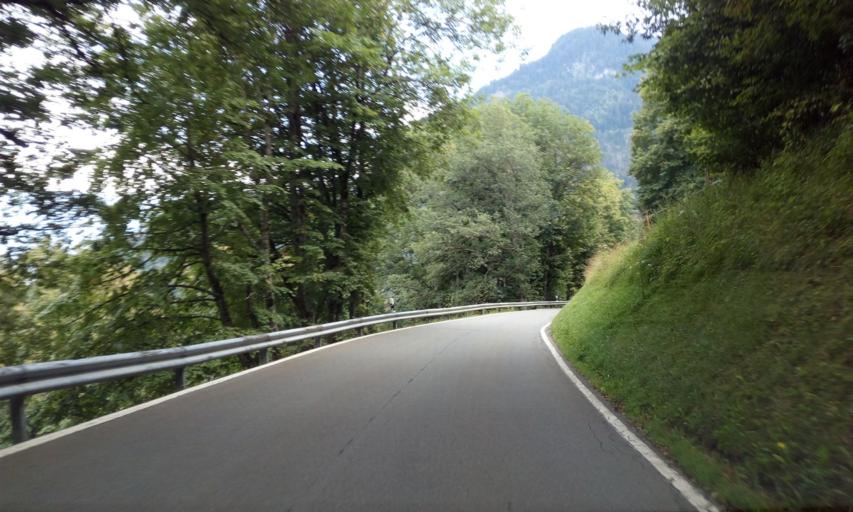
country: CH
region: Valais
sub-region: Monthey District
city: Vionnaz
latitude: 46.3075
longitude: 6.8855
